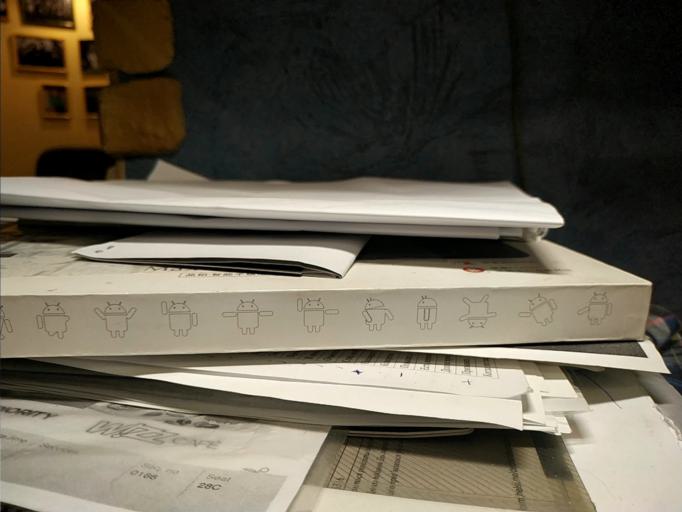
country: RU
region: Tverskaya
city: Zubtsov
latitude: 56.0861
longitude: 34.7684
